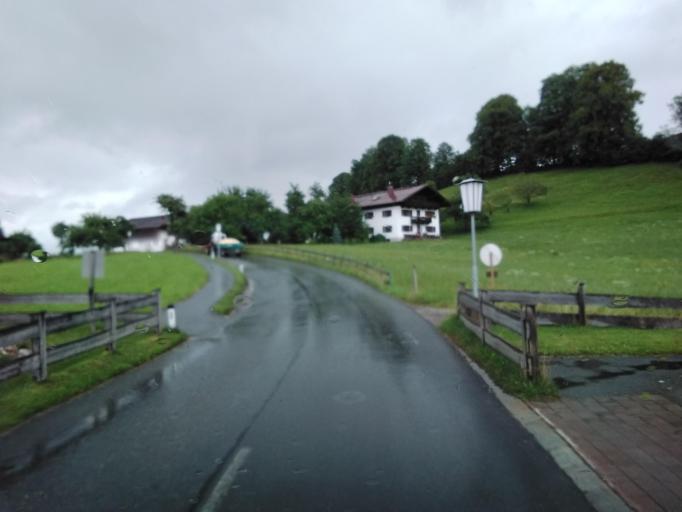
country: AT
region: Tyrol
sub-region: Politischer Bezirk Kitzbuhel
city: Schwendt
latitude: 47.6353
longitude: 12.3919
